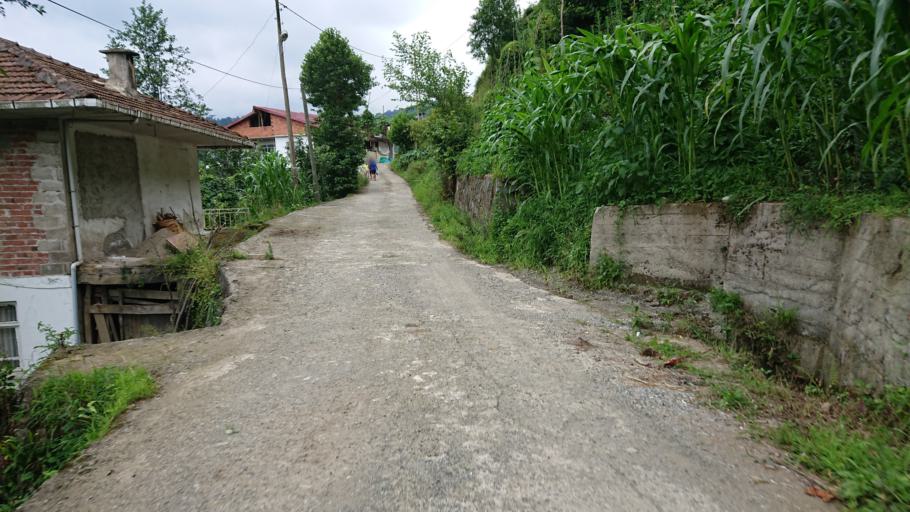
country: TR
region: Rize
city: Rize
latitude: 40.9695
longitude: 40.5146
